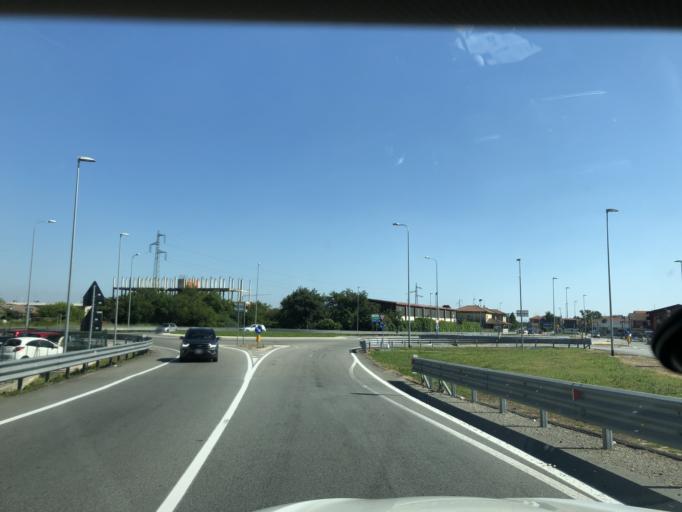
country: IT
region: Piedmont
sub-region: Provincia di Novara
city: Oleggio
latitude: 45.6005
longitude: 8.6444
